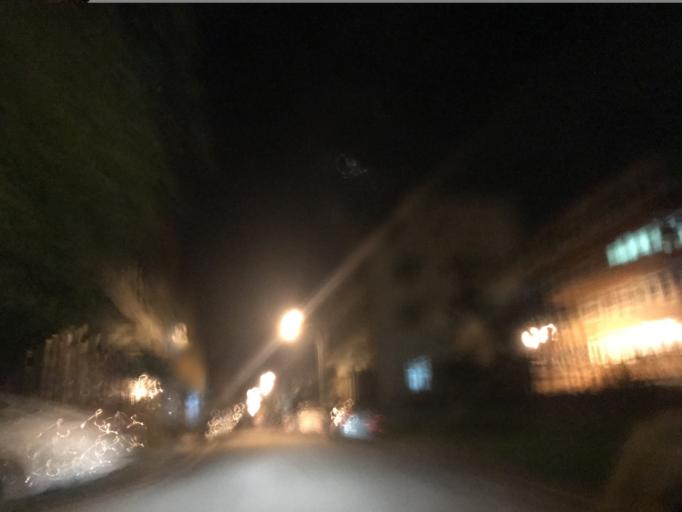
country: TW
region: Taiwan
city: Daxi
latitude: 24.8517
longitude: 121.2180
